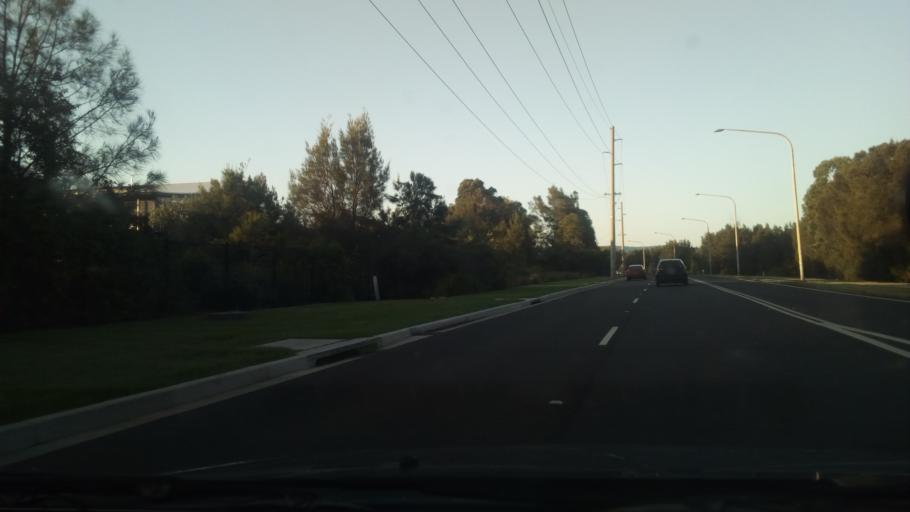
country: AU
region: New South Wales
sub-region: Wollongong
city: Fairy Meadow
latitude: -34.4009
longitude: 150.9006
